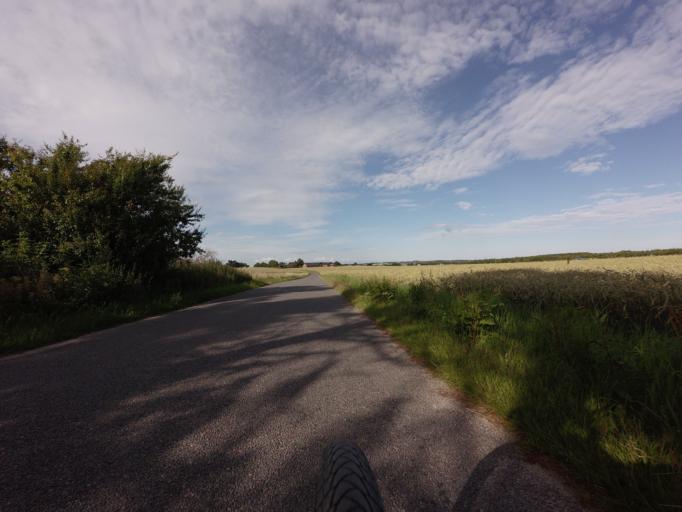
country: DK
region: Central Jutland
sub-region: Skanderborg Kommune
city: Horning
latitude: 56.0929
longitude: 10.0136
